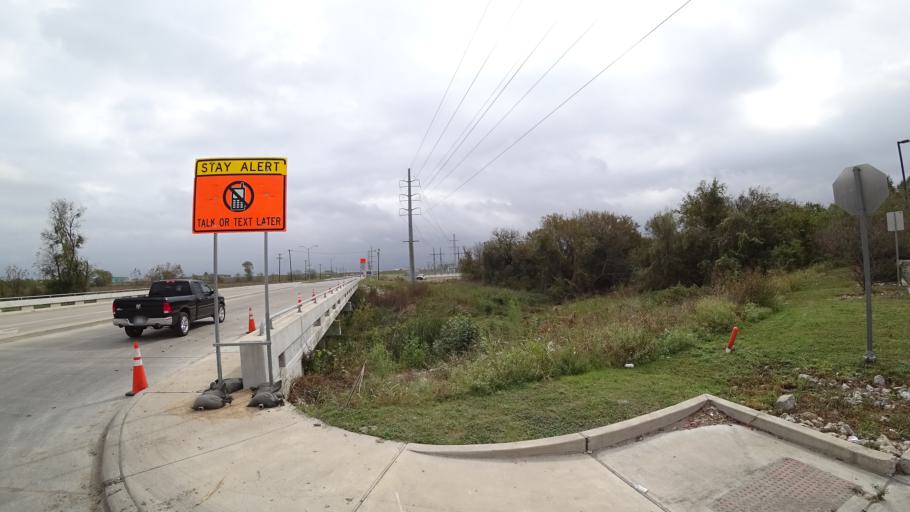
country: US
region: Texas
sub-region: Travis County
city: Pflugerville
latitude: 30.4553
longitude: -97.6013
